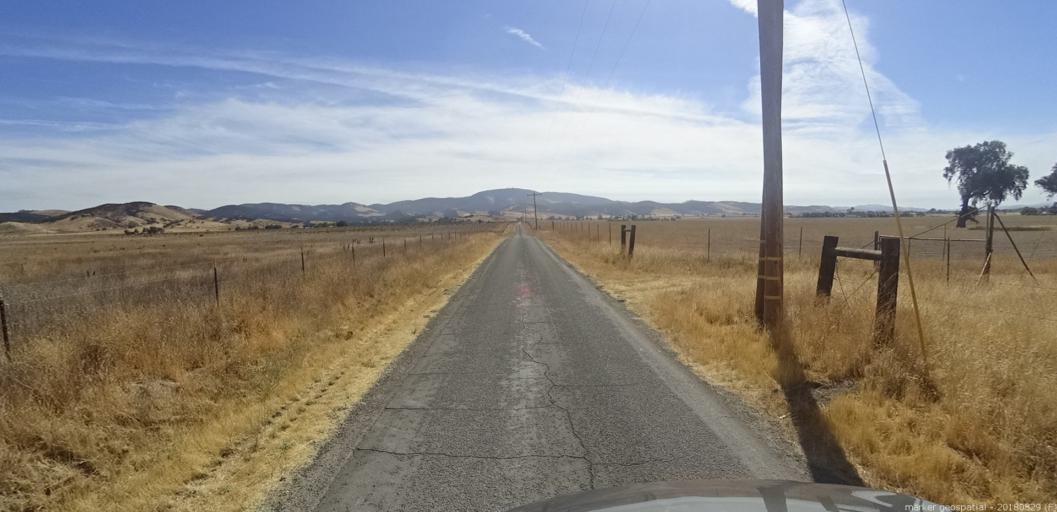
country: US
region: California
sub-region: Monterey County
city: King City
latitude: 35.9514
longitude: -121.0895
